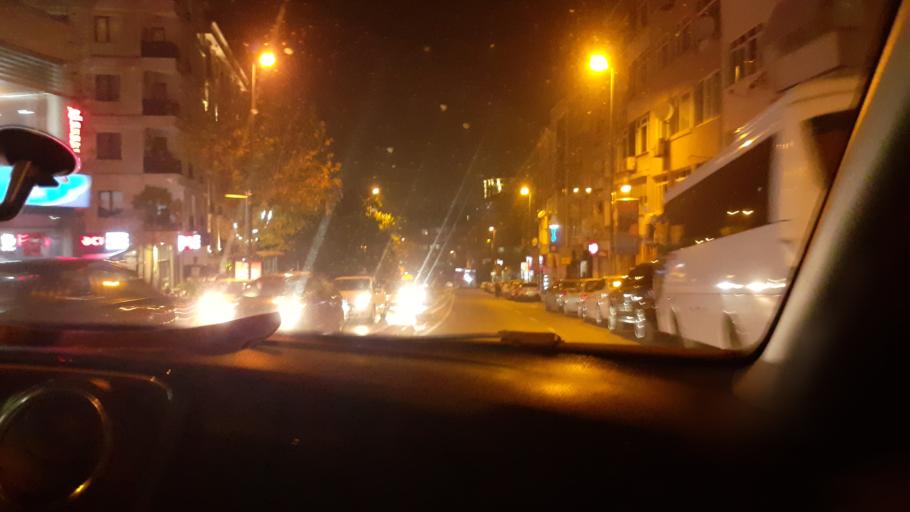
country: TR
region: Istanbul
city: UEskuedar
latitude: 41.0278
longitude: 29.0304
